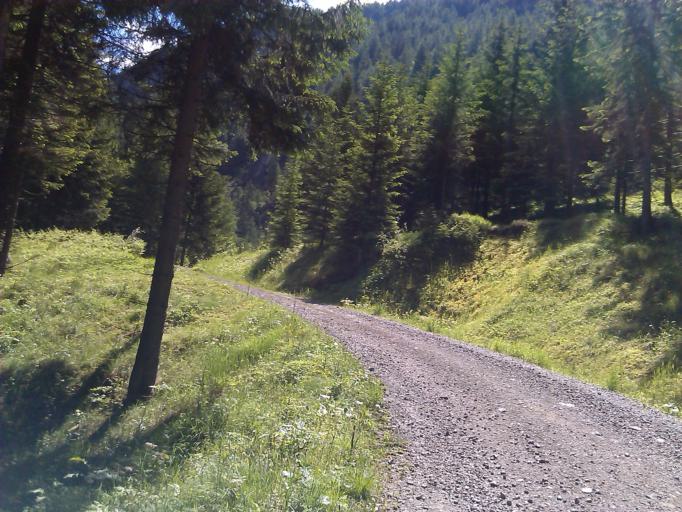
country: AT
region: Tyrol
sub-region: Politischer Bezirk Imst
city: Nassereith
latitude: 47.3549
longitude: 10.8520
